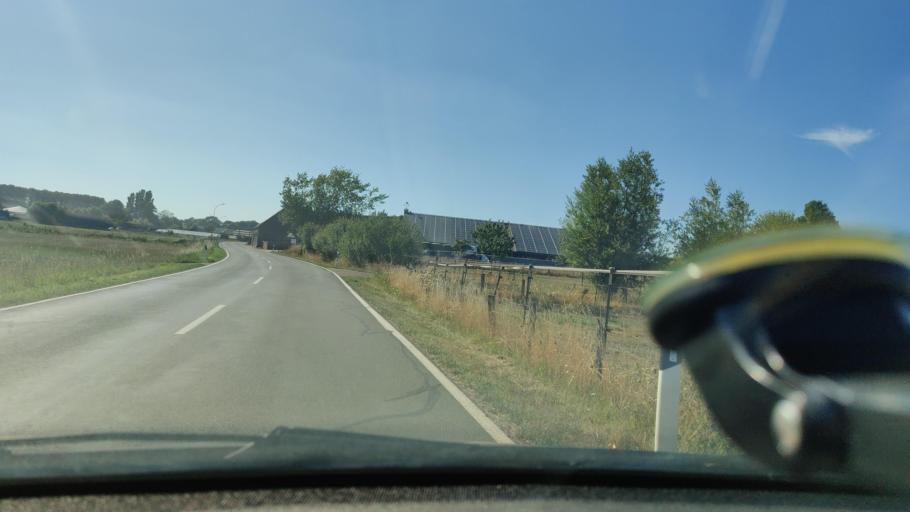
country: DE
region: North Rhine-Westphalia
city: Geldern
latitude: 51.4695
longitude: 6.3470
